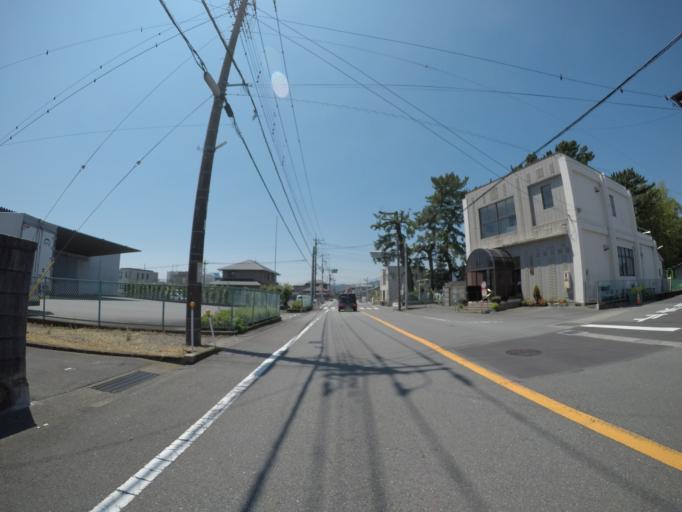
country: JP
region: Shizuoka
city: Fuji
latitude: 35.1420
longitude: 138.6390
